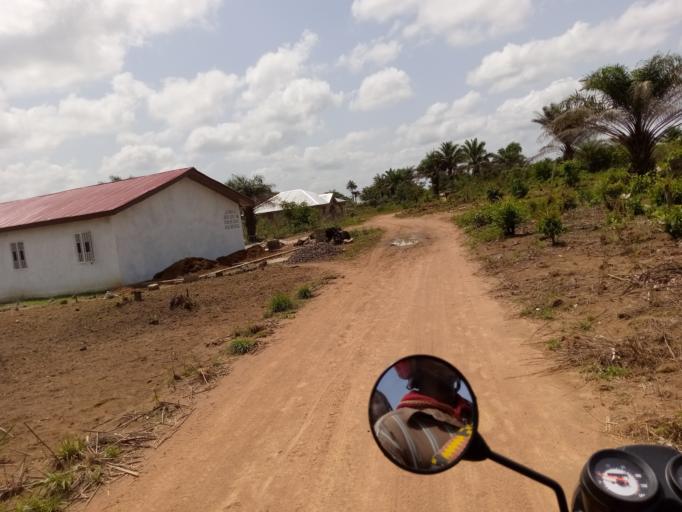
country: SL
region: Western Area
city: Waterloo
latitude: 8.3556
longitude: -13.0064
